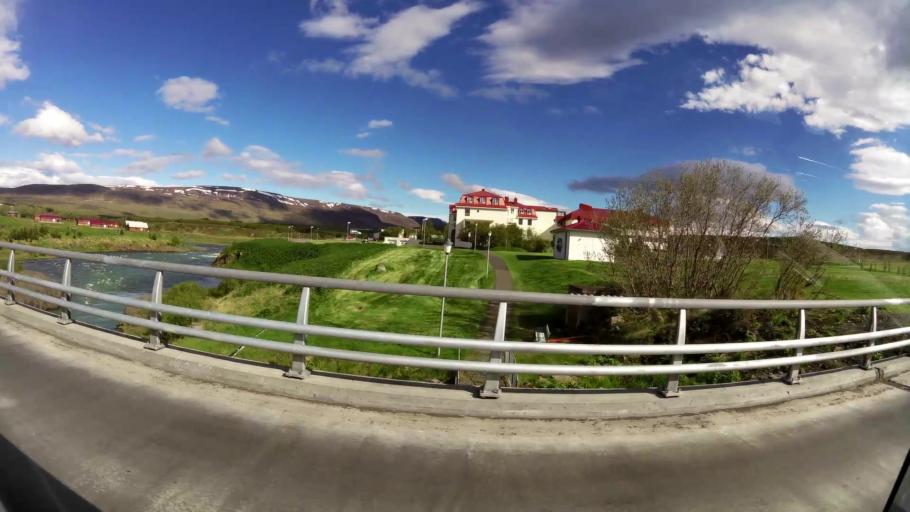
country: IS
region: Northwest
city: Saudarkrokur
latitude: 65.6572
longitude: -20.2826
